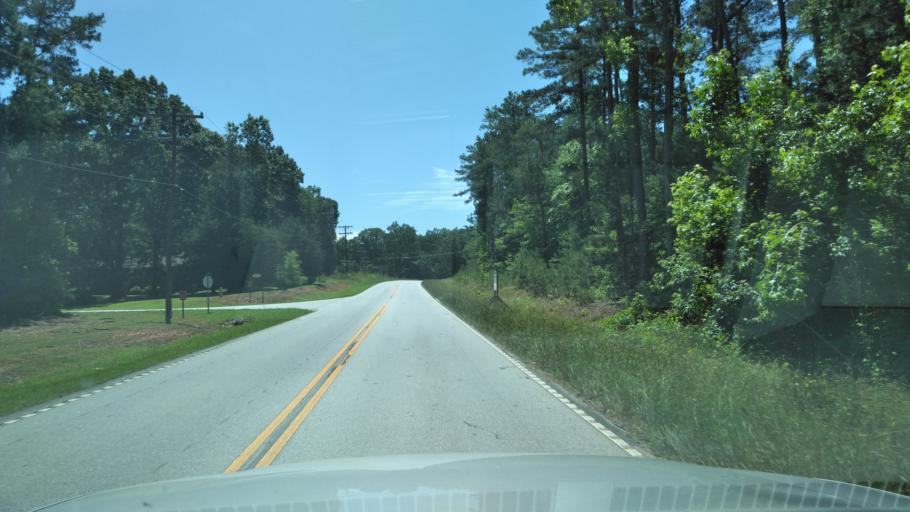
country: US
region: South Carolina
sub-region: Laurens County
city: Laurens
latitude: 34.4977
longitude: -82.0566
